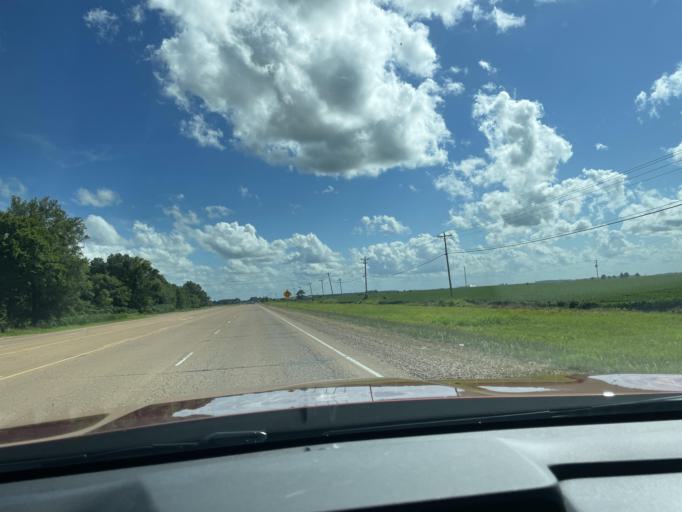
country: US
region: Mississippi
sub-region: Humphreys County
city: Belzoni
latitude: 33.1584
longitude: -90.5020
